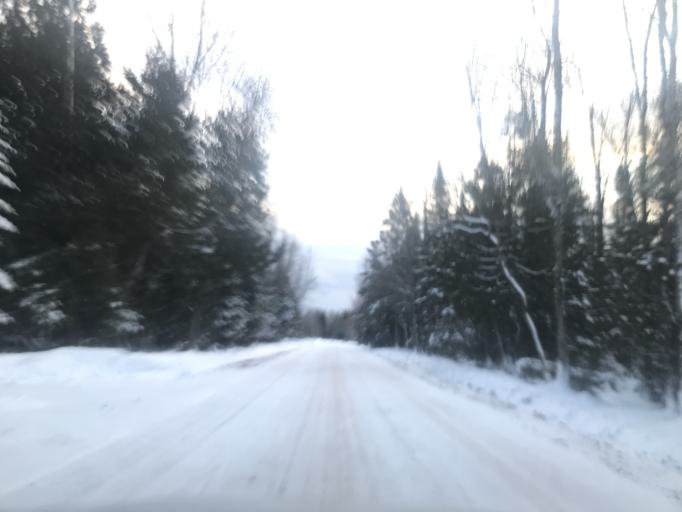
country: US
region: Michigan
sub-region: Menominee County
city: Menominee
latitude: 45.4184
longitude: -87.3376
